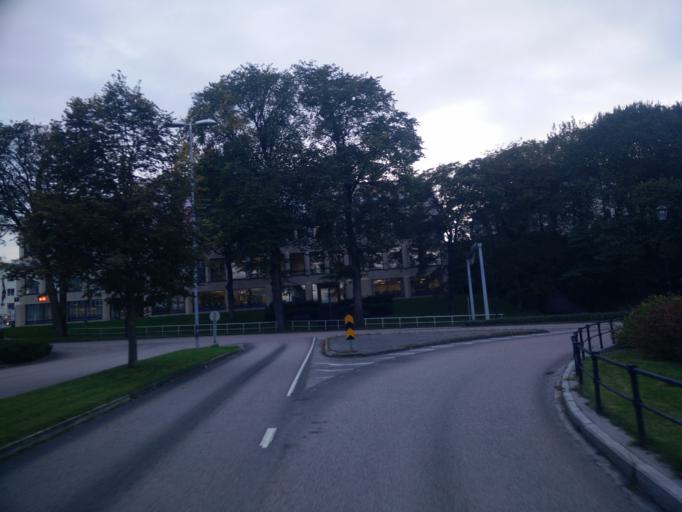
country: NO
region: More og Romsdal
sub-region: Kristiansund
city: Kristiansund
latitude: 63.1107
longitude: 7.7288
